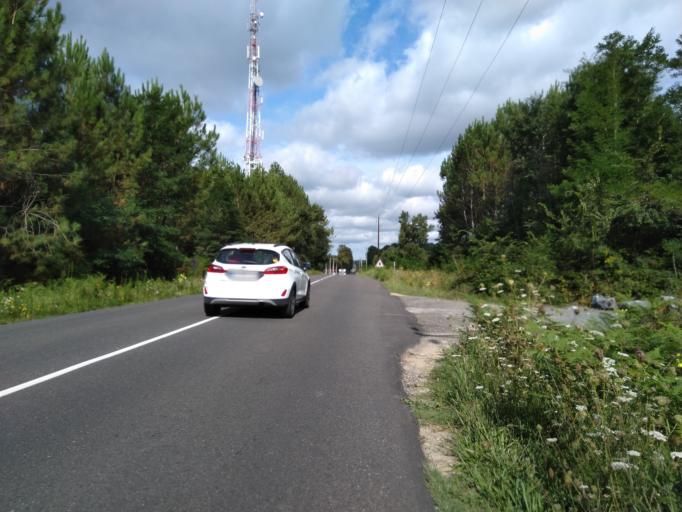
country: FR
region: Aquitaine
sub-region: Departement des Landes
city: Mees
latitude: 43.7334
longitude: -1.1054
